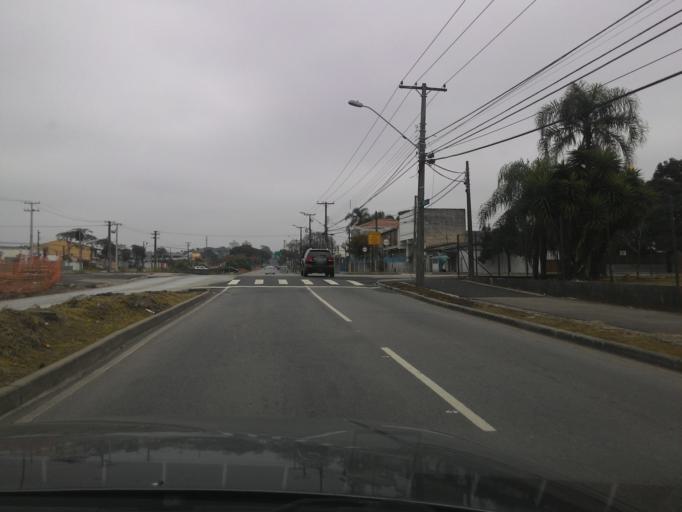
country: BR
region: Parana
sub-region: Curitiba
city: Curitiba
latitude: -25.4710
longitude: -49.2588
